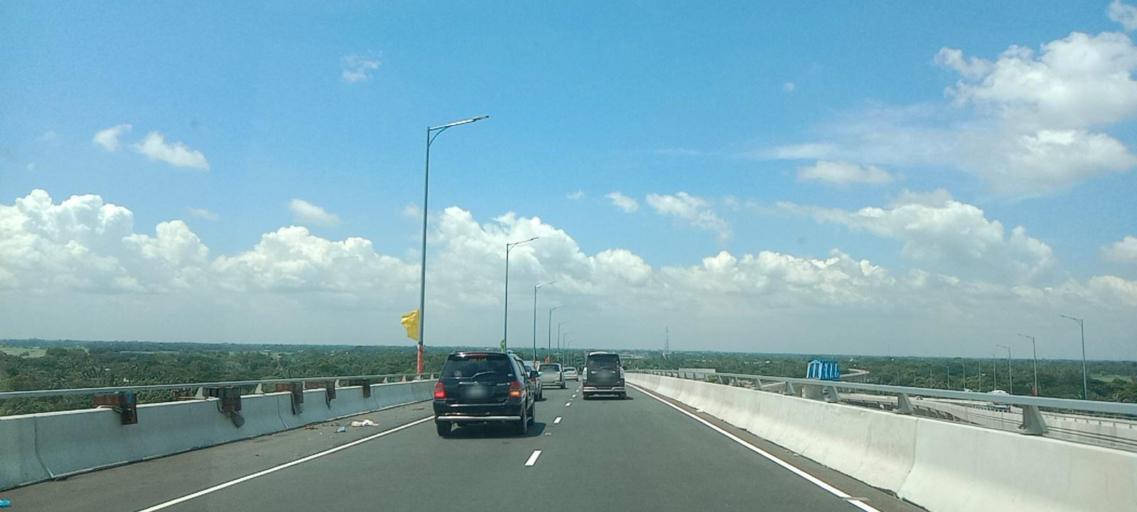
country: BD
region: Dhaka
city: Char Bhadrasan
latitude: 23.4725
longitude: 90.2649
